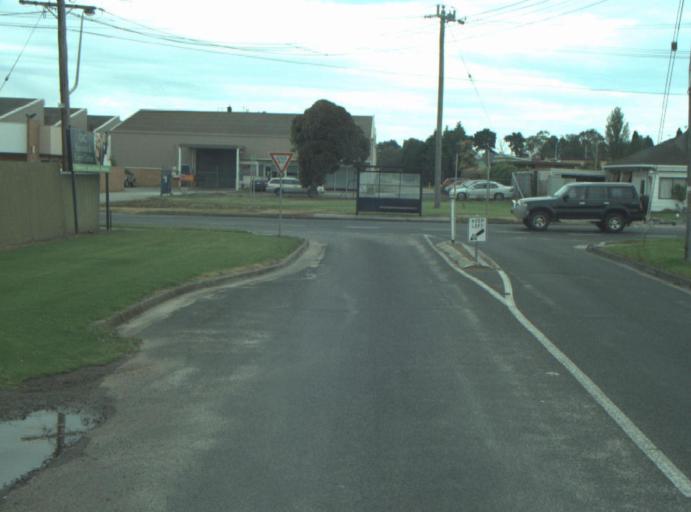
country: AU
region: Victoria
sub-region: Greater Geelong
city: Breakwater
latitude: -38.1790
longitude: 144.3707
